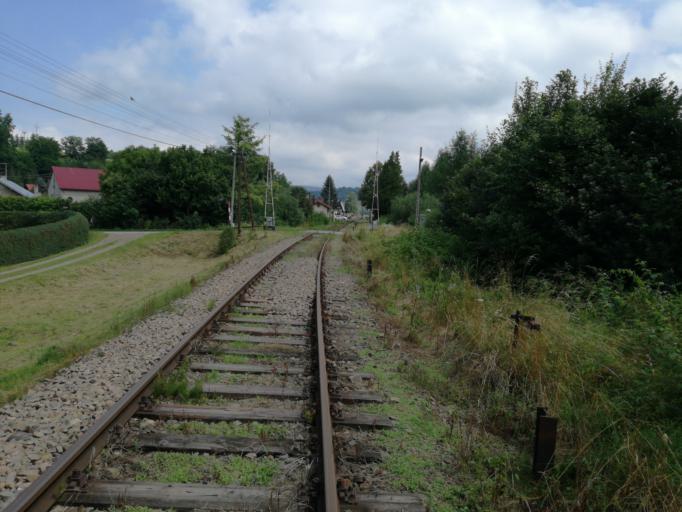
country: PL
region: Subcarpathian Voivodeship
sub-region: Powiat leski
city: Uherce Mineralne
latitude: 49.4631
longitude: 22.3971
